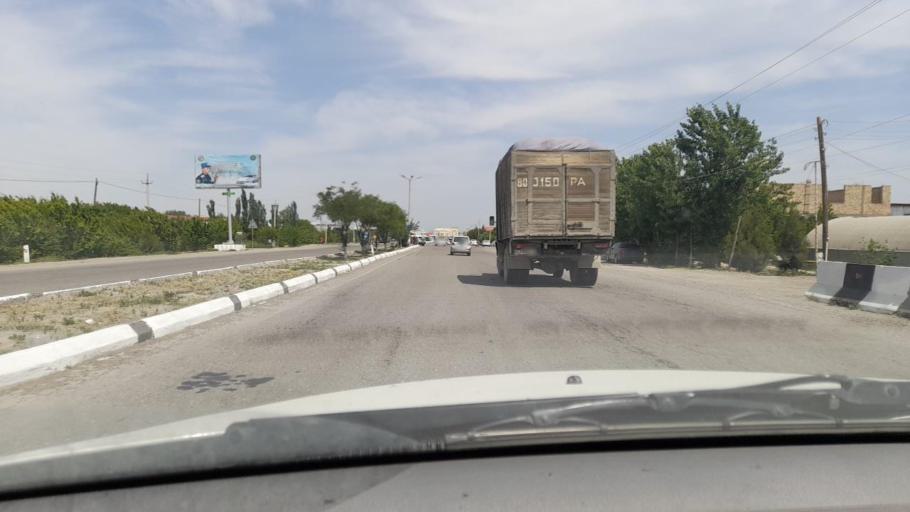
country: UZ
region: Bukhara
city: Wobkent
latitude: 40.0098
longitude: 64.5261
